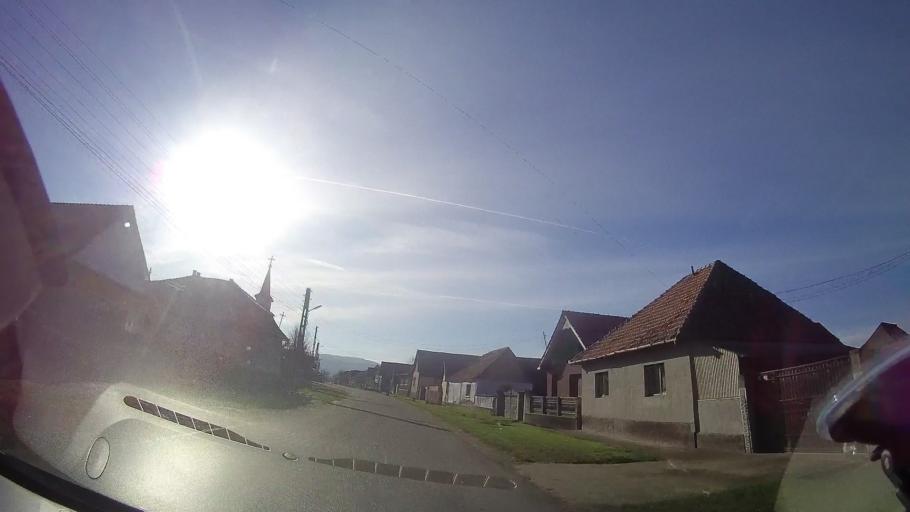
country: RO
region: Bihor
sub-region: Comuna Auseu
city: Grosi
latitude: 47.0240
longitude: 22.4722
